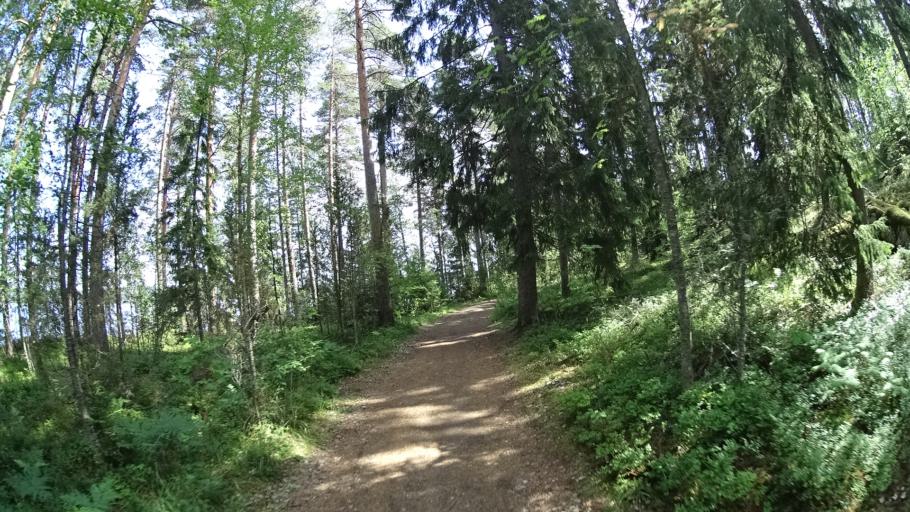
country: FI
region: Haeme
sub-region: Forssa
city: Tammela
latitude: 60.7764
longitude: 23.8540
